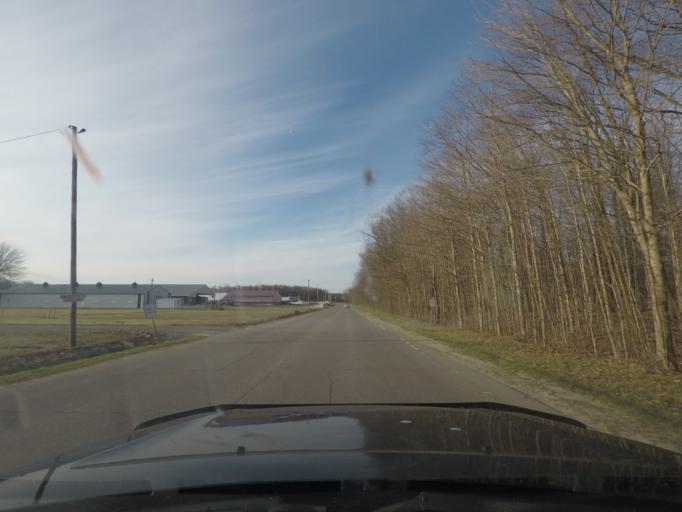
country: US
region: Indiana
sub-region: LaPorte County
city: LaPorte
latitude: 41.5940
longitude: -86.7492
